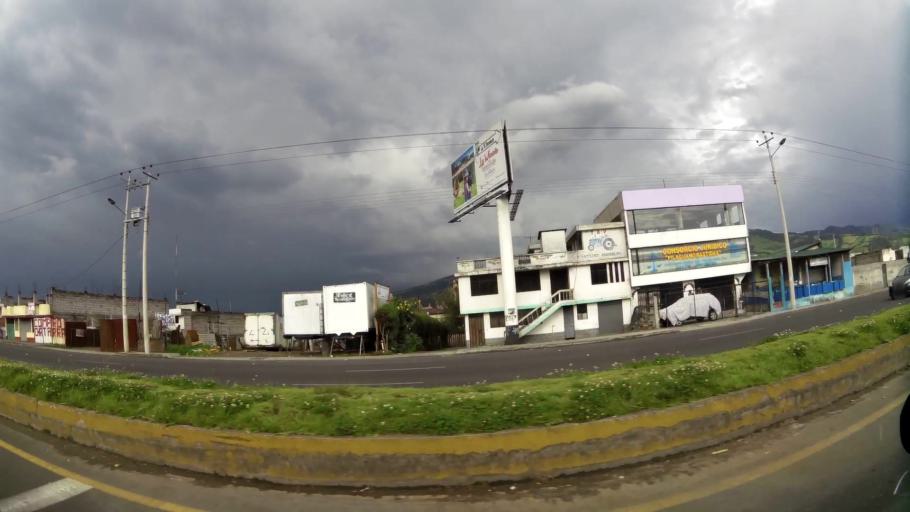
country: EC
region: Pichincha
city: Machachi
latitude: -0.4096
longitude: -78.5474
